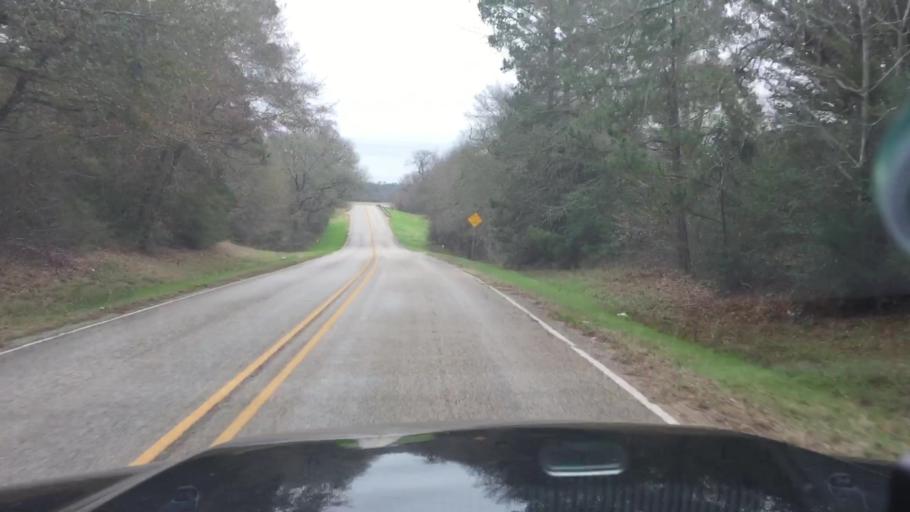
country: US
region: Texas
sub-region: Fayette County
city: La Grange
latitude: 30.0118
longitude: -96.9196
